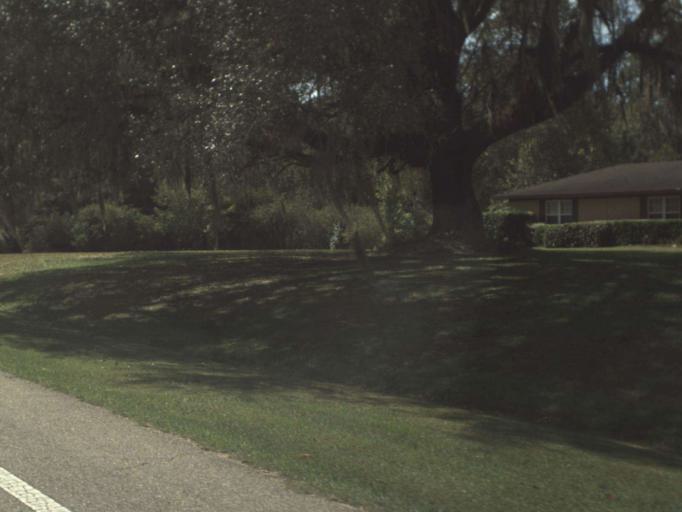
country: US
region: Florida
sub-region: Jackson County
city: Graceville
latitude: 30.8699
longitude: -85.5266
